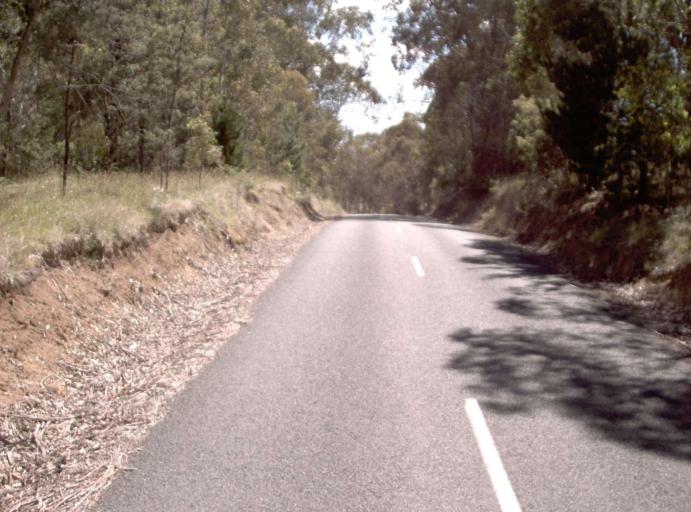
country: AU
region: New South Wales
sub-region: Bombala
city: Bombala
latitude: -37.0572
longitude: 148.8038
